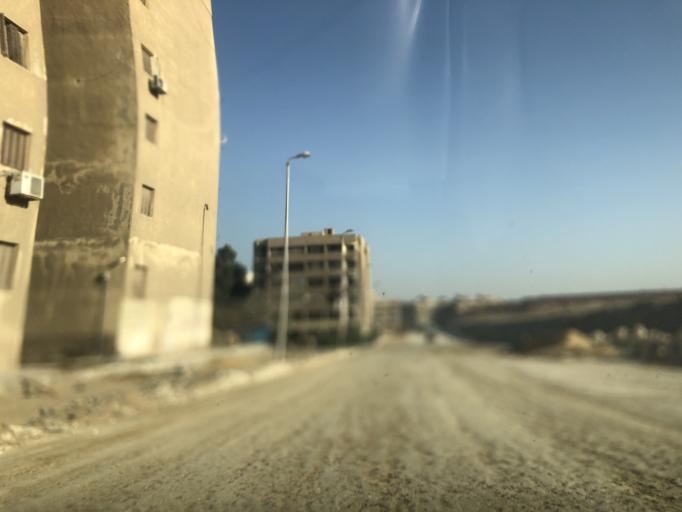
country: EG
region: Al Jizah
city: Al Jizah
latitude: 29.9890
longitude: 31.1115
